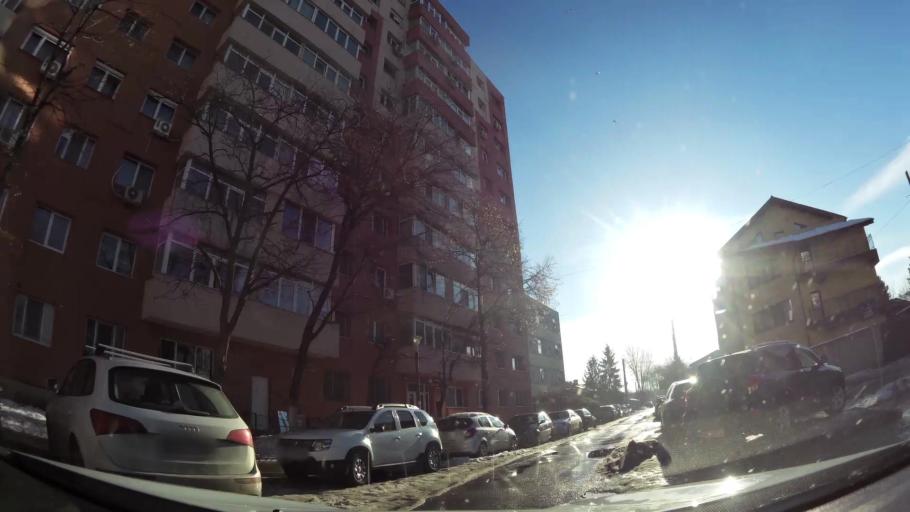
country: RO
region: Bucuresti
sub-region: Municipiul Bucuresti
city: Bucuresti
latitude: 44.3936
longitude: 26.0911
